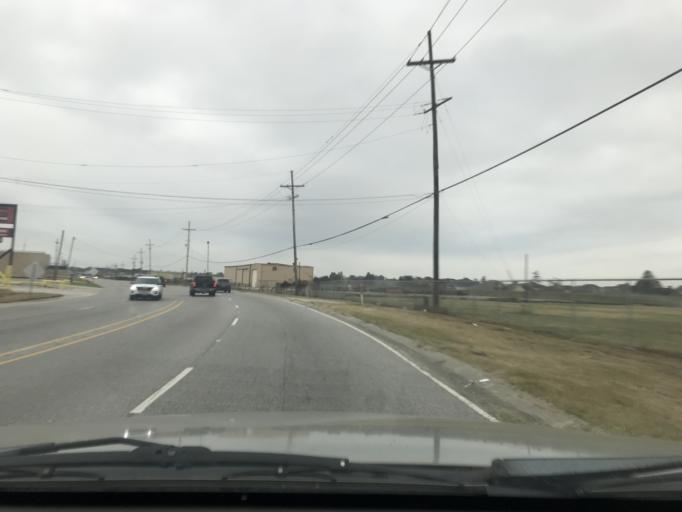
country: US
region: Louisiana
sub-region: Jefferson Parish
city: Harvey
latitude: 29.8819
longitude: -90.0758
